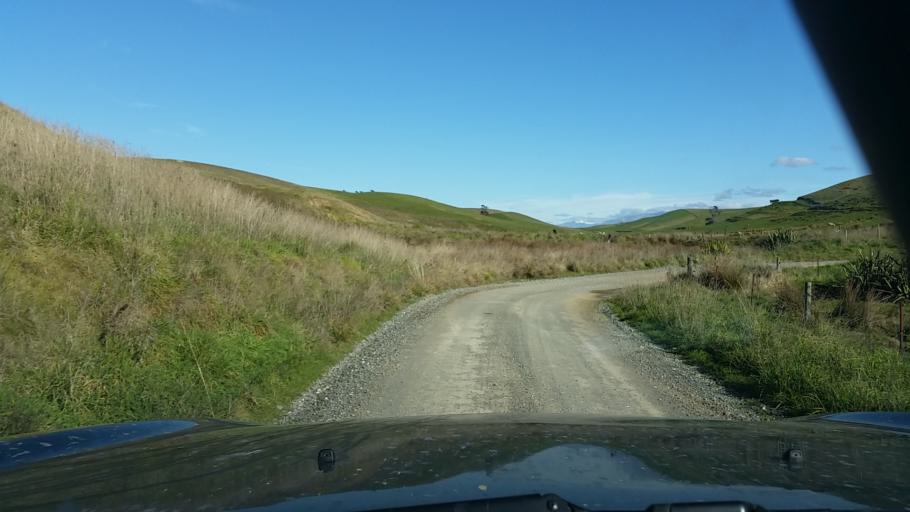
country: NZ
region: Marlborough
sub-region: Marlborough District
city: Blenheim
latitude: -41.6708
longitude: 174.1304
